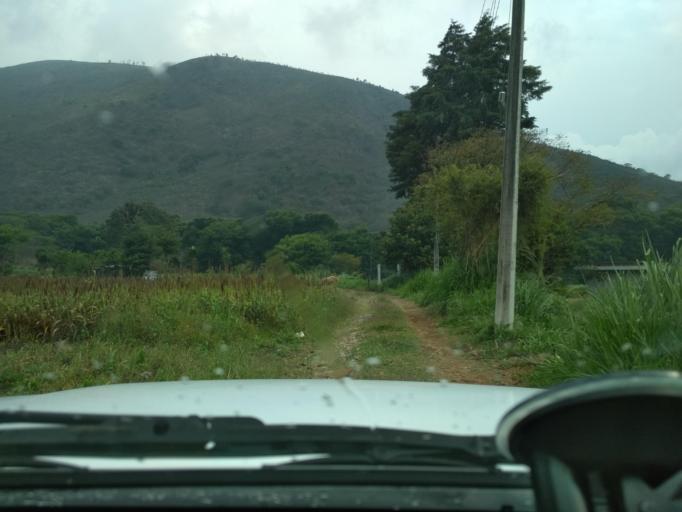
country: MX
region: Veracruz
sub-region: Nogales
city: Taza de Agua Ojo Zarco
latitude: 18.7782
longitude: -97.2052
